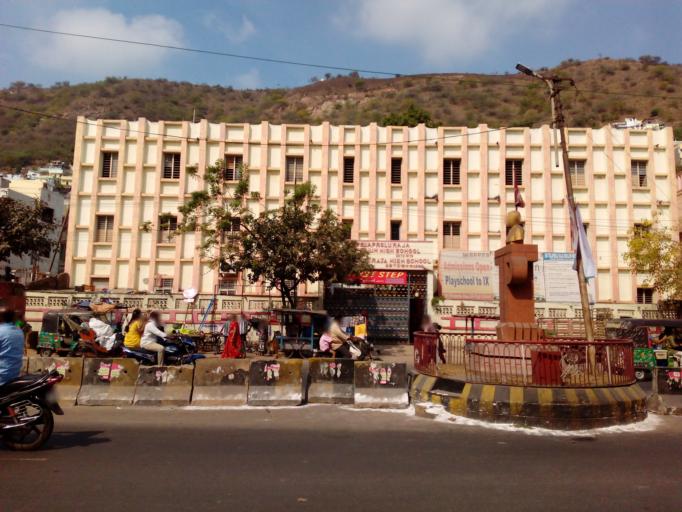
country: IN
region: Andhra Pradesh
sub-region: Krishna
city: Vijayawada
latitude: 16.5231
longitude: 80.6115
